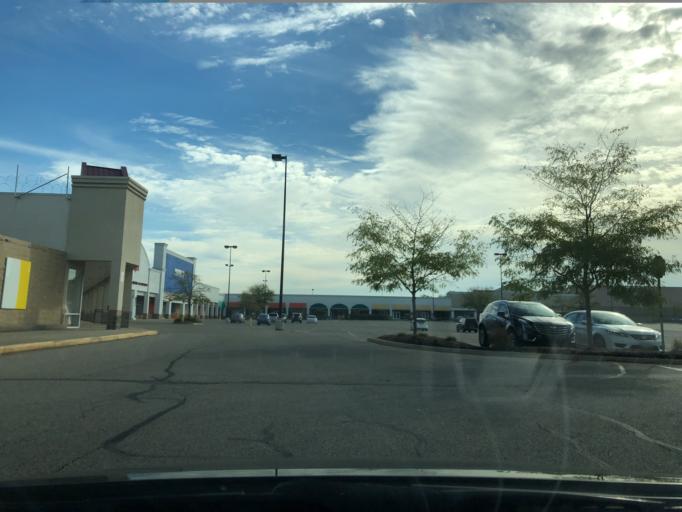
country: US
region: Ohio
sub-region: Hamilton County
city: Glendale
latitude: 39.2900
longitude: -84.4590
